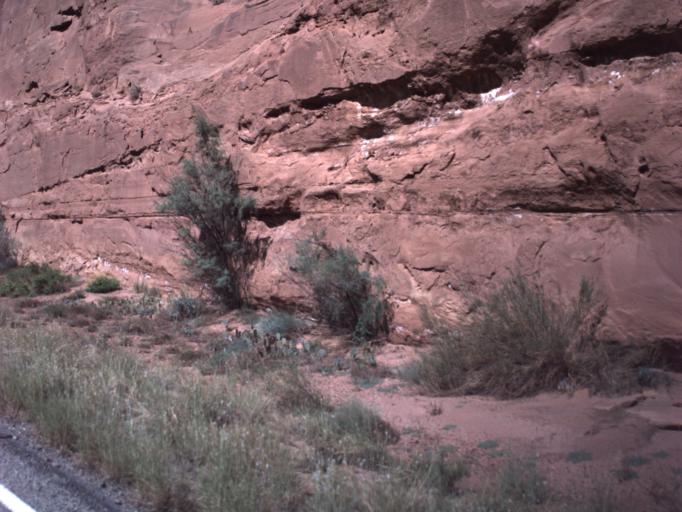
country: US
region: Utah
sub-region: Grand County
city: Moab
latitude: 38.5355
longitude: -109.6276
